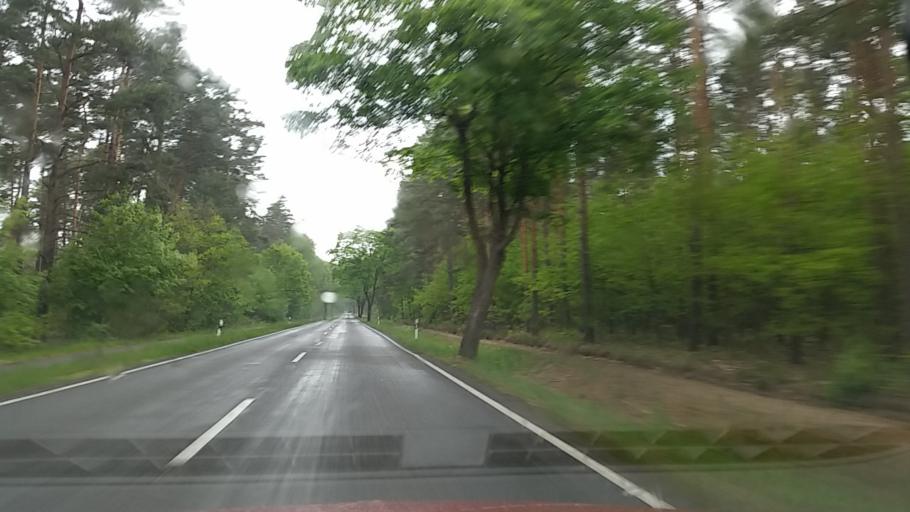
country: DE
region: Brandenburg
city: Grunheide
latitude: 52.3773
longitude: 13.8333
